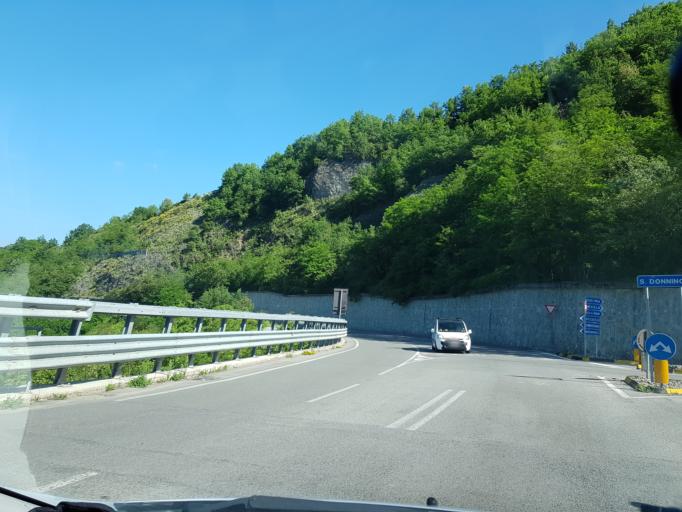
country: IT
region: Tuscany
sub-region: Provincia di Lucca
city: Piazza al Serchio-San Michele
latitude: 44.1828
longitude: 10.3086
